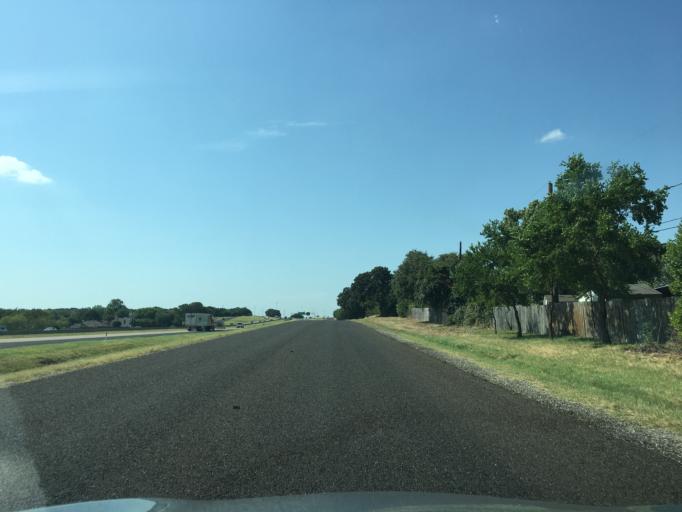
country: US
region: Texas
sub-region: Tarrant County
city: Kennedale
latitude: 32.6588
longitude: -97.1949
